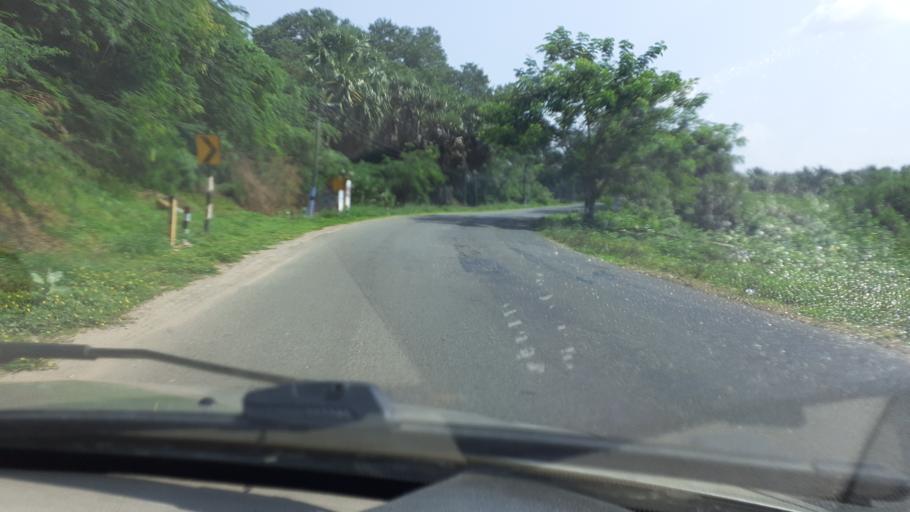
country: IN
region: Tamil Nadu
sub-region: Thoothukkudi
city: Srivaikuntam
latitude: 8.6323
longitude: 77.8797
